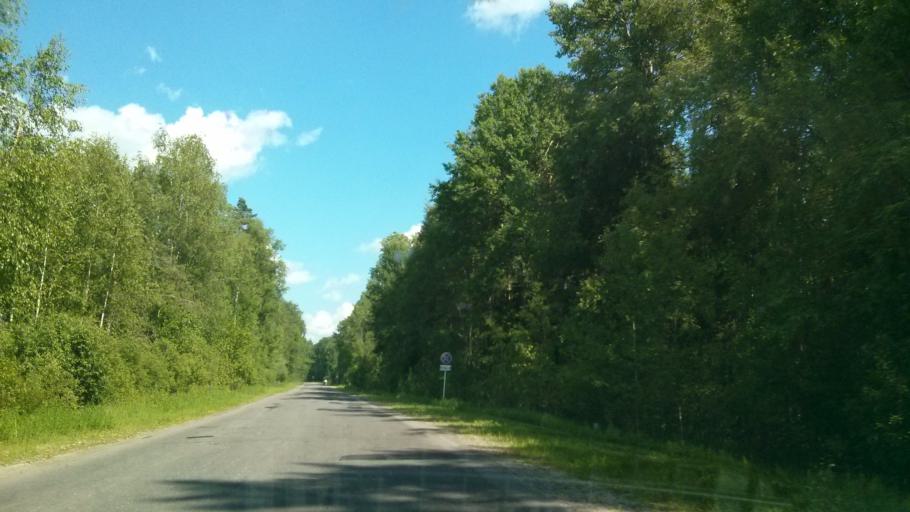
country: RU
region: Vladimir
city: Melenki
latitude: 55.3321
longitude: 41.6867
